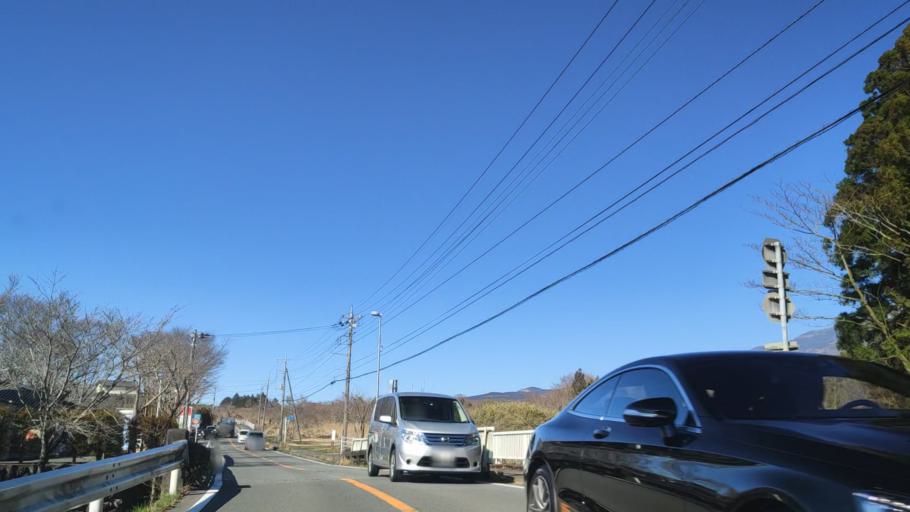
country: JP
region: Shizuoka
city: Fujinomiya
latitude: 35.3277
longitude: 138.5938
